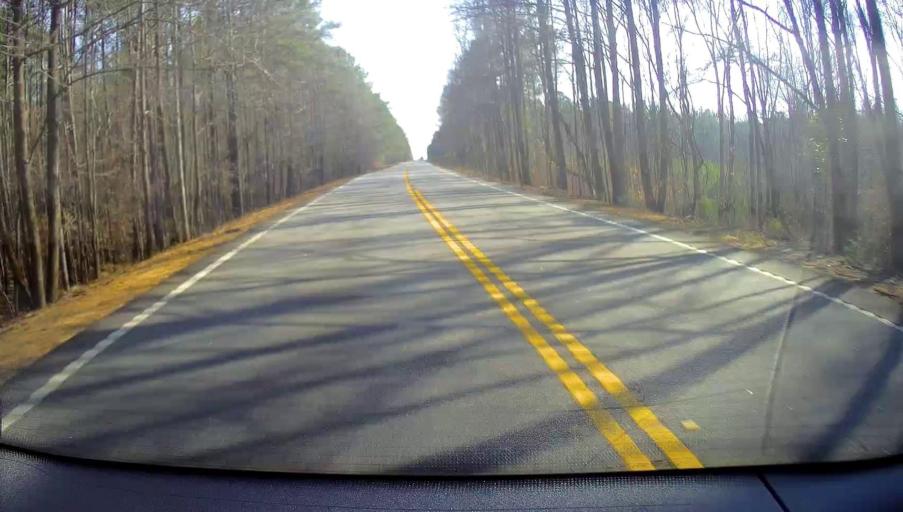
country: US
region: Georgia
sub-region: Butts County
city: Indian Springs
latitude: 33.1919
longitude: -83.8486
